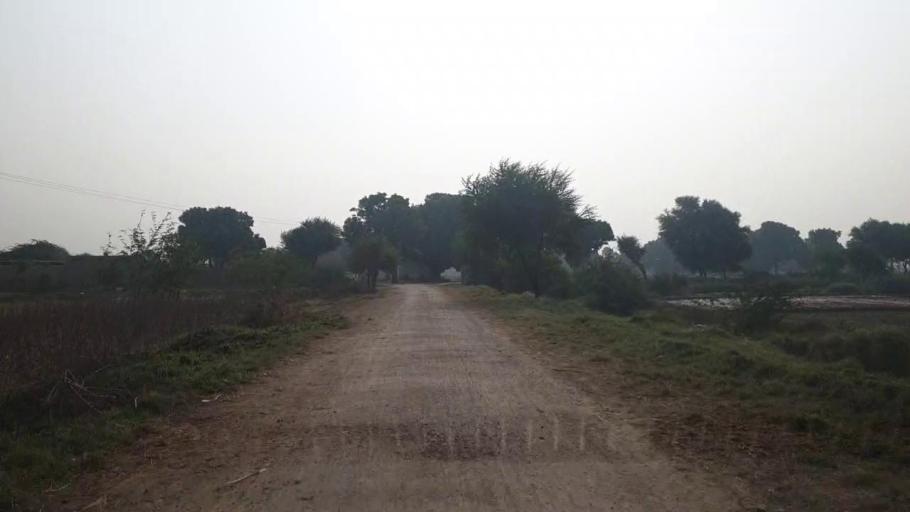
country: PK
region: Sindh
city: Tando Jam
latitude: 25.3208
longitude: 68.5196
